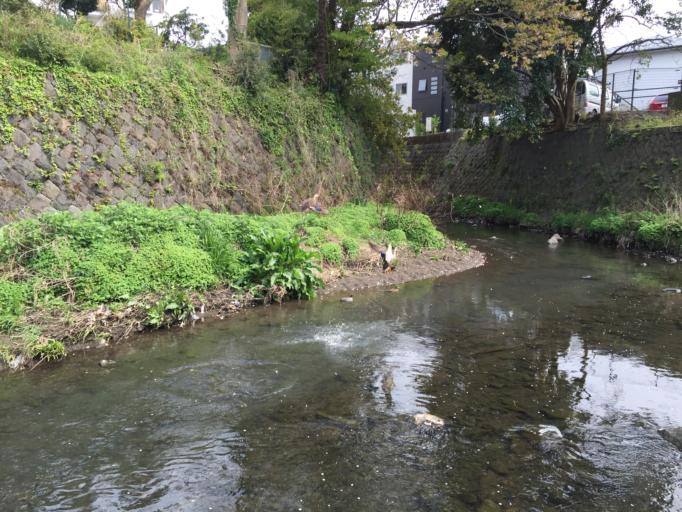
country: JP
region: Kanagawa
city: Yokohama
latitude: 35.4046
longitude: 139.5930
